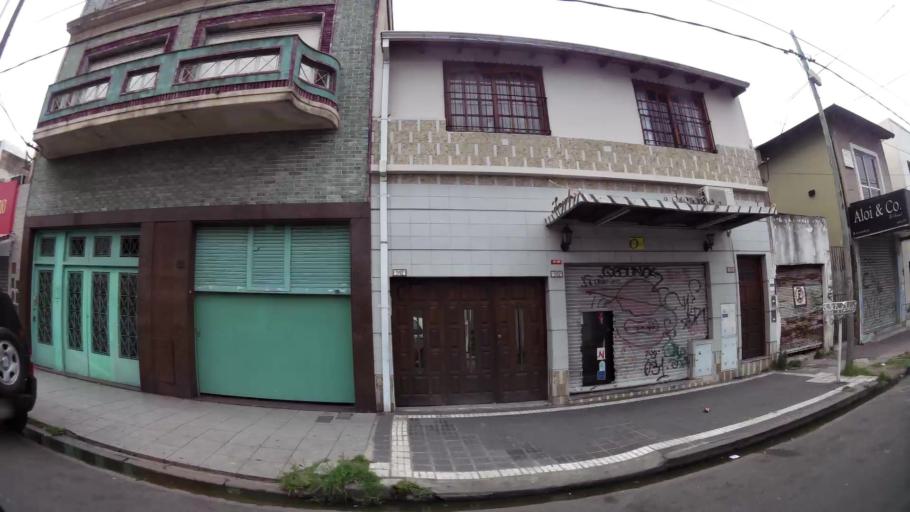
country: AR
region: Buenos Aires
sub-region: Partido de Lanus
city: Lanus
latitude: -34.6858
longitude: -58.3751
